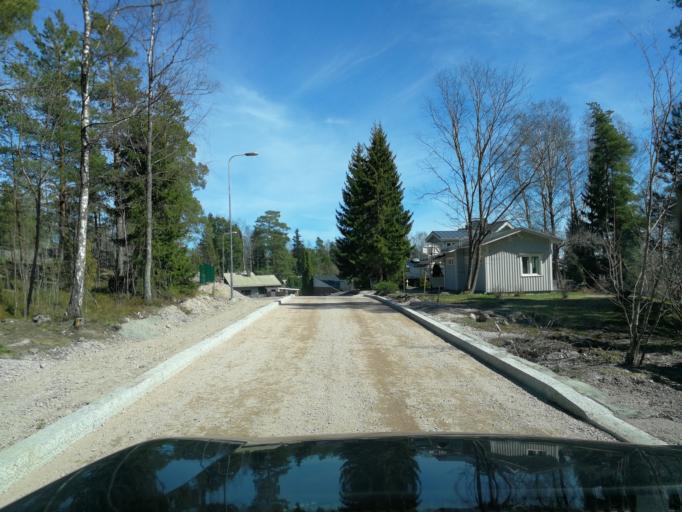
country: FI
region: Uusimaa
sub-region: Helsinki
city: Espoo
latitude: 60.1640
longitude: 24.6907
